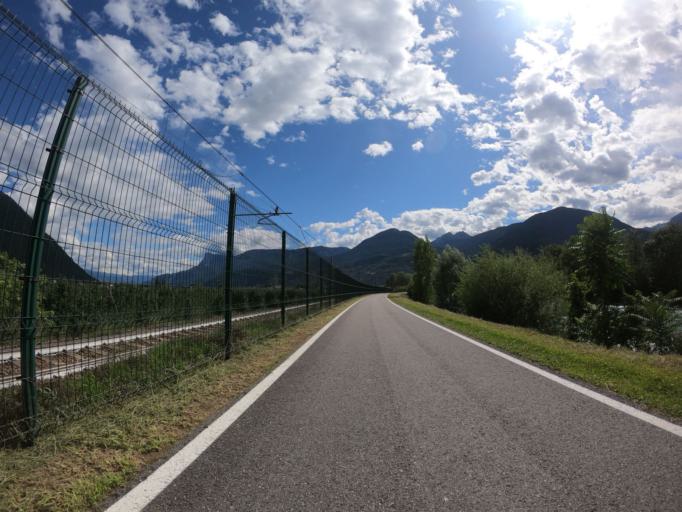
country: IT
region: Trentino-Alto Adige
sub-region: Bolzano
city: Postal
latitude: 46.6146
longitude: 11.1838
